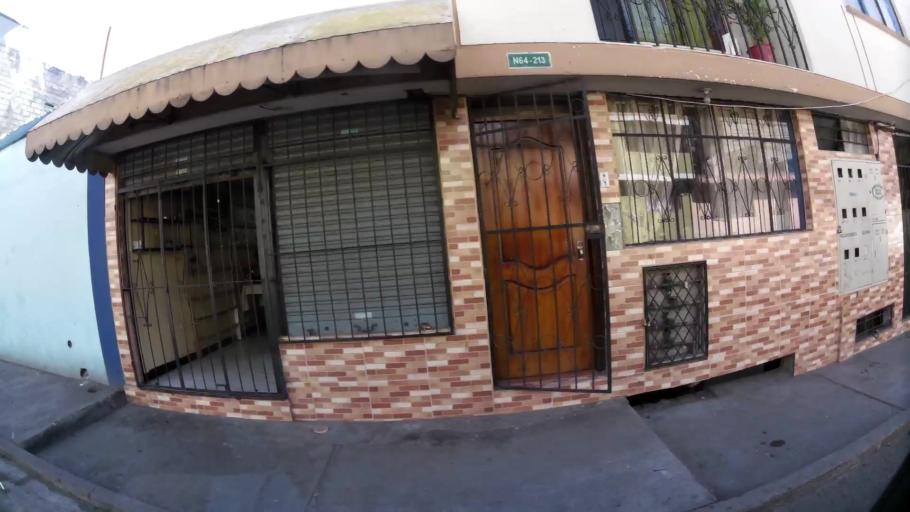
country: EC
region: Pichincha
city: Quito
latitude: -0.1206
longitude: -78.4699
